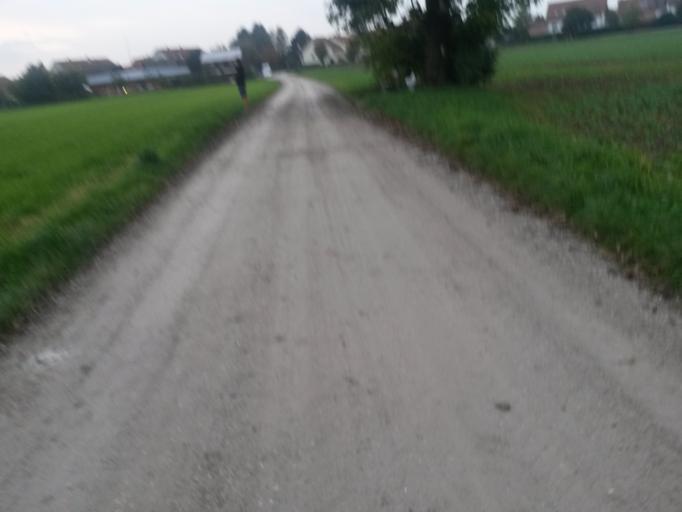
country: DE
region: Bavaria
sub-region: Upper Bavaria
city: Grasbrunn
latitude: 48.0815
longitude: 11.7472
